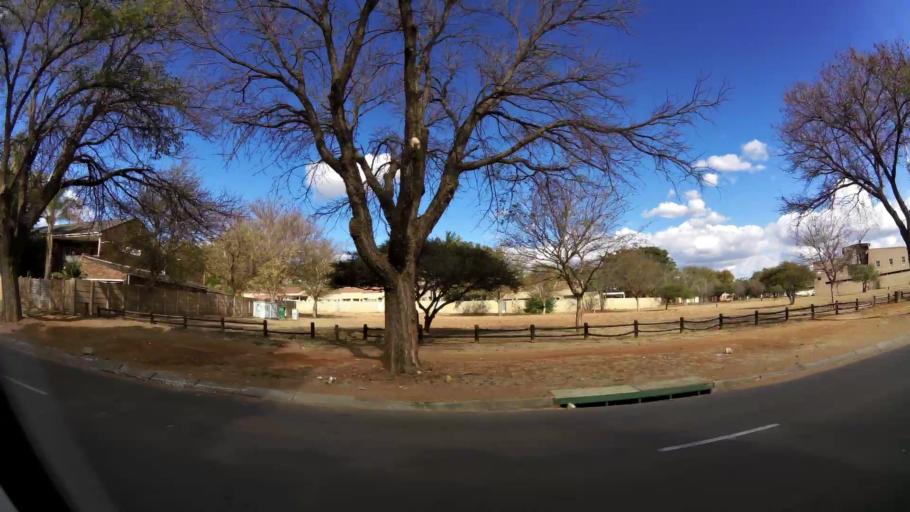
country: ZA
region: Limpopo
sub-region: Capricorn District Municipality
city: Polokwane
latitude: -23.8933
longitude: 29.4708
